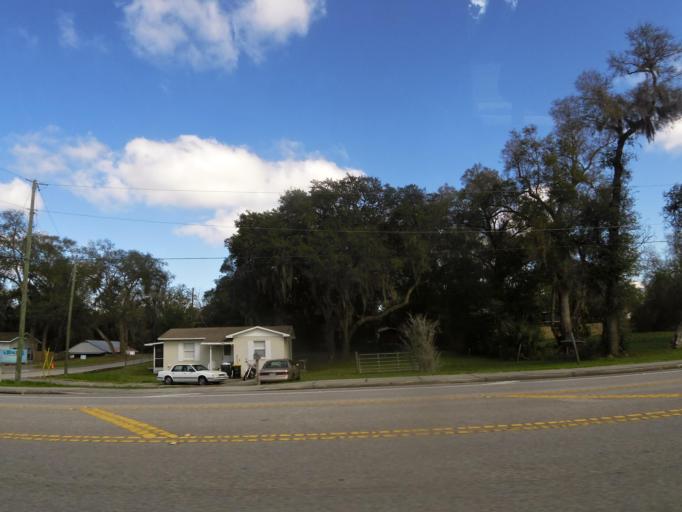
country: US
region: Florida
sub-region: Volusia County
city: Orange City
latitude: 28.9340
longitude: -81.3007
